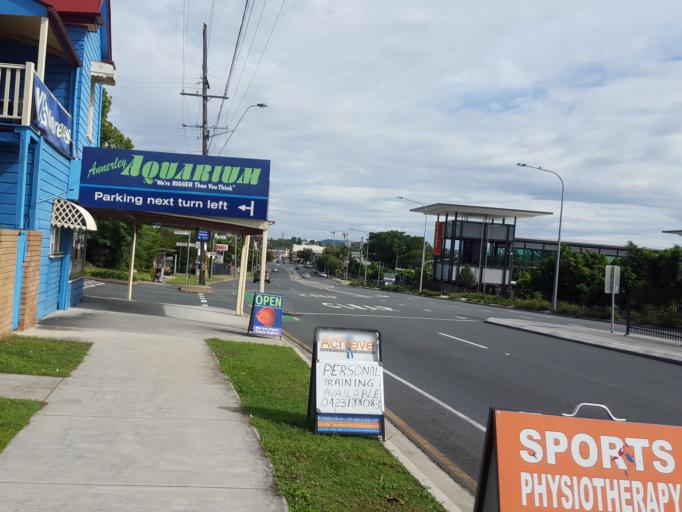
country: AU
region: Queensland
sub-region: Brisbane
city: Greenslopes
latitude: -27.4990
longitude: 153.0505
